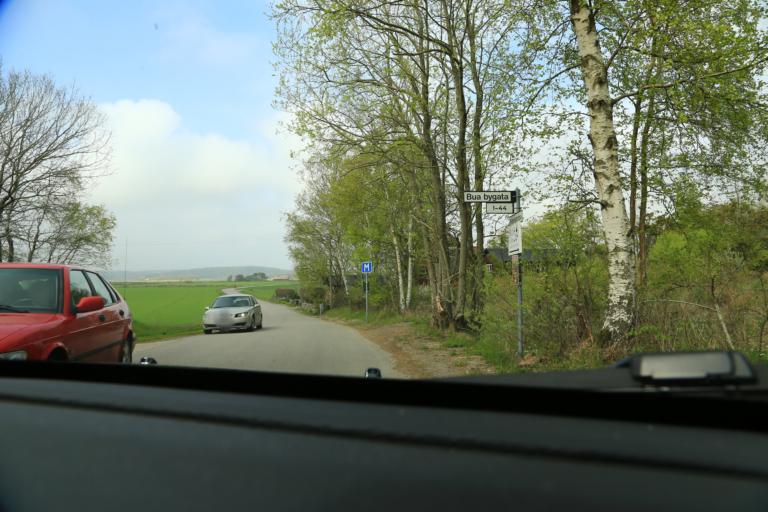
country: SE
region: Halland
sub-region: Kungsbacka Kommun
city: Frillesas
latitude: 57.2267
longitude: 12.1545
